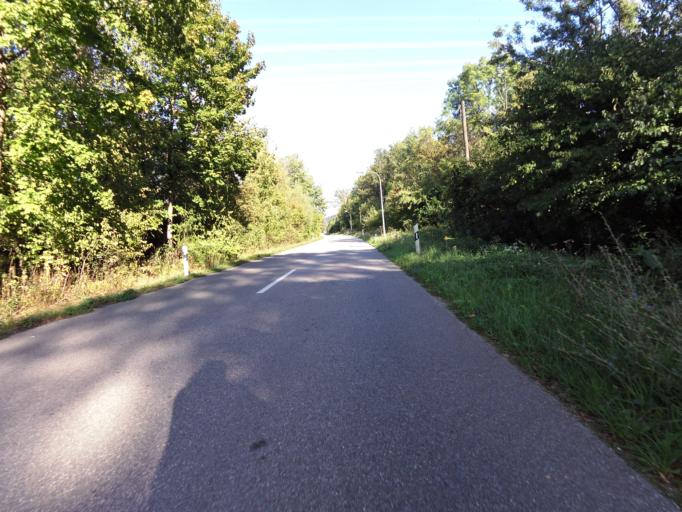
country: DE
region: Bavaria
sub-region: Lower Bavaria
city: Niederaichbach
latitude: 48.6044
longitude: 12.3068
